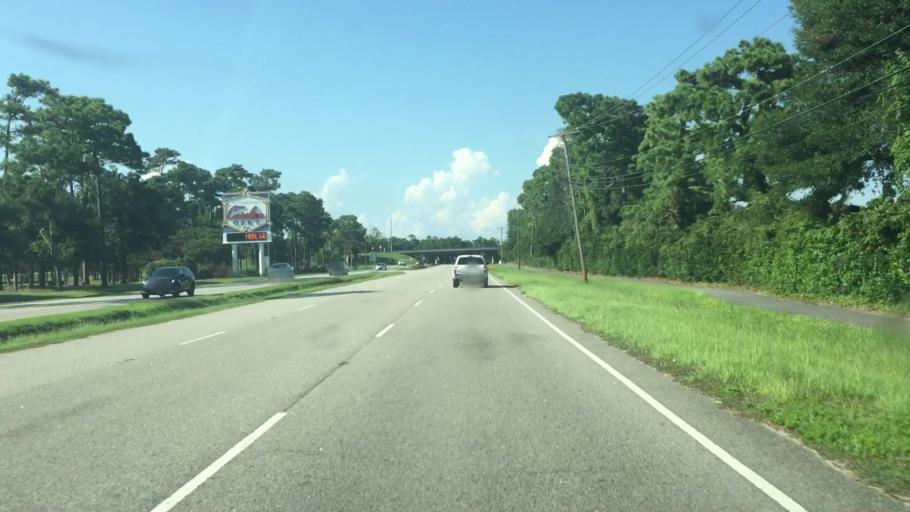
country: US
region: South Carolina
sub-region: Horry County
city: Myrtle Beach
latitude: 33.7636
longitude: -78.8059
